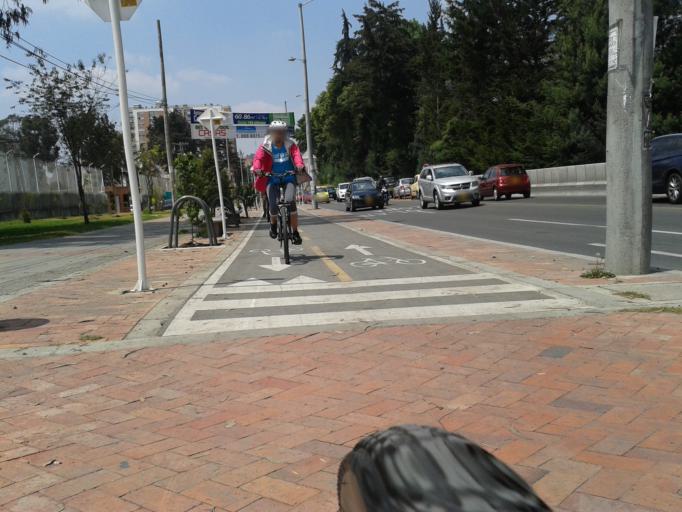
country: CO
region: Bogota D.C.
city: Barrio San Luis
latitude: 4.7384
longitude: -74.0521
